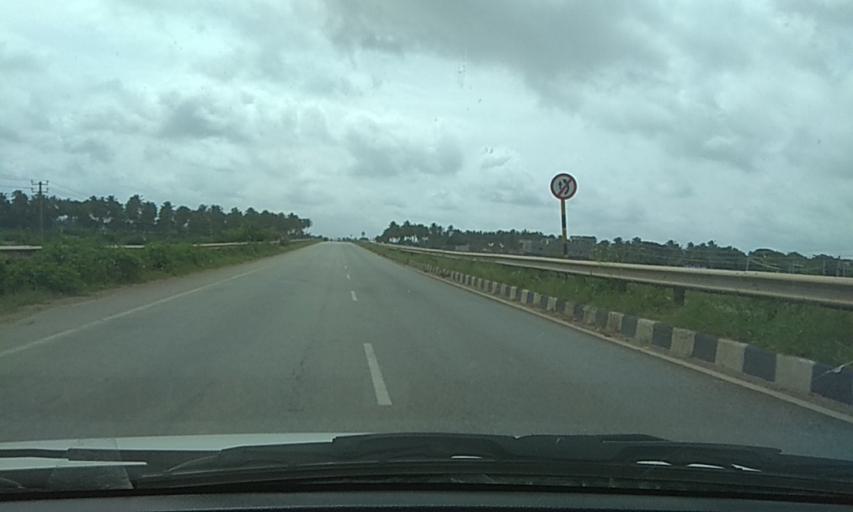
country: IN
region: Karnataka
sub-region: Davanagere
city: Harihar
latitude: 14.4528
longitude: 75.8730
